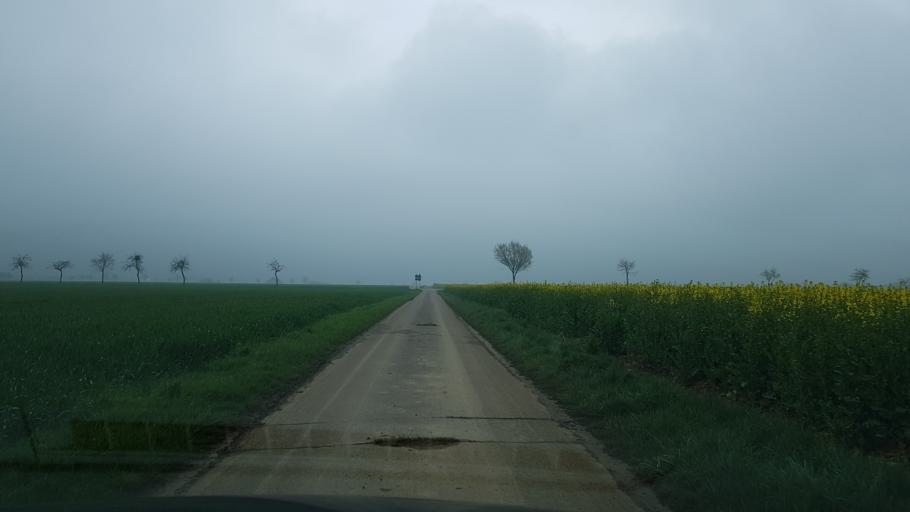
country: DE
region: North Rhine-Westphalia
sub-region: Regierungsbezirk Detmold
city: Paderborn
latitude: 51.6202
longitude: 8.7357
